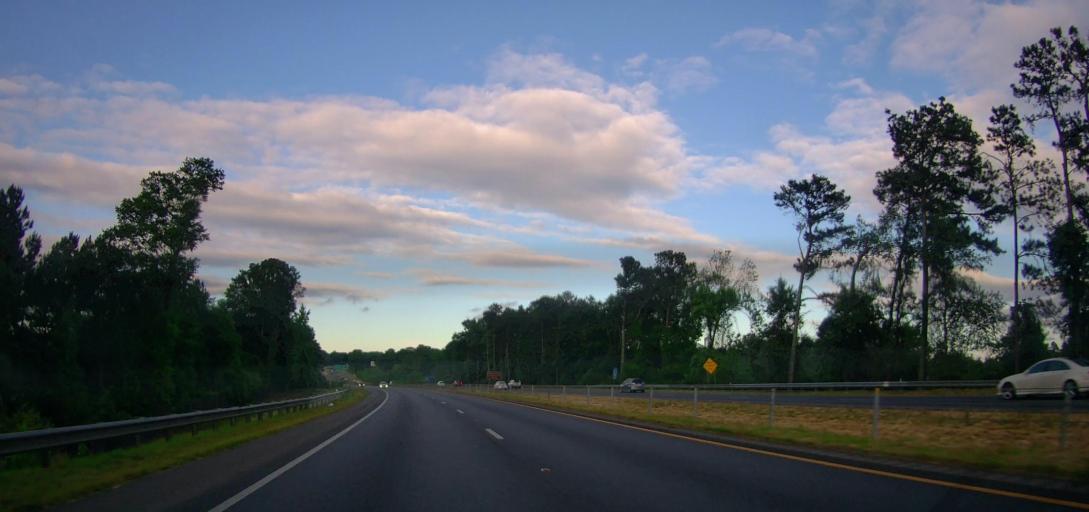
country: US
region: Georgia
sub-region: Clarke County
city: Athens
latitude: 33.9755
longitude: -83.3861
